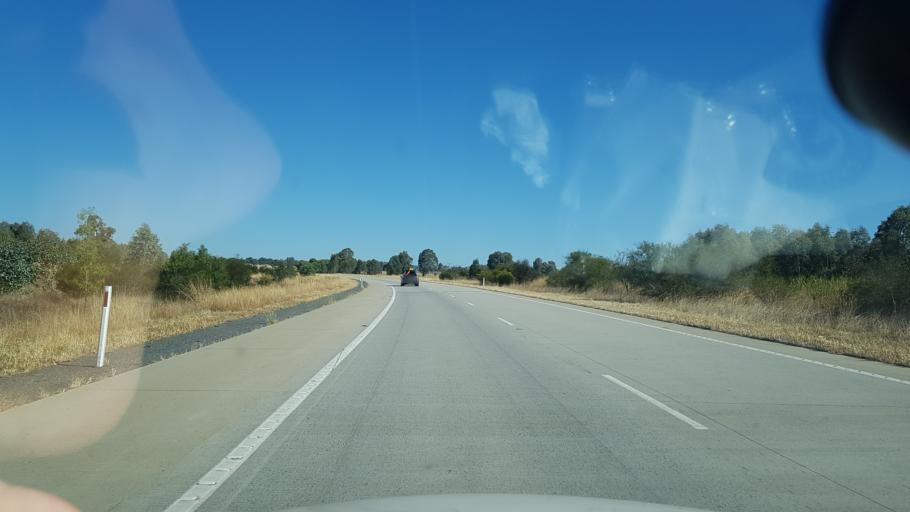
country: AU
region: New South Wales
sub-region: Greater Hume Shire
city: Jindera
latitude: -35.9301
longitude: 147.0040
